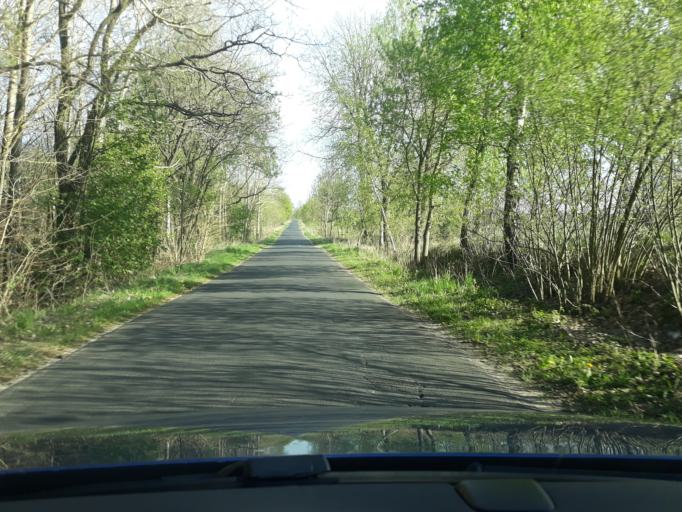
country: PL
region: Pomeranian Voivodeship
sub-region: Powiat czluchowski
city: Przechlewo
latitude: 53.8563
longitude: 17.3495
